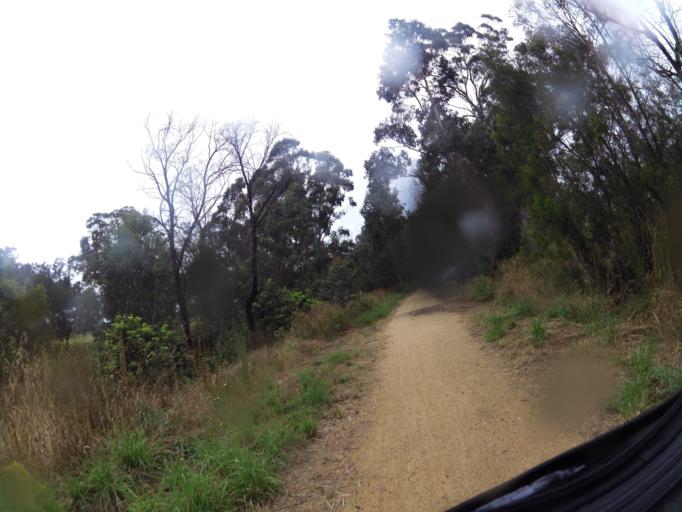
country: AU
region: Victoria
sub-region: East Gippsland
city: Lakes Entrance
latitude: -37.7652
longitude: 147.8209
